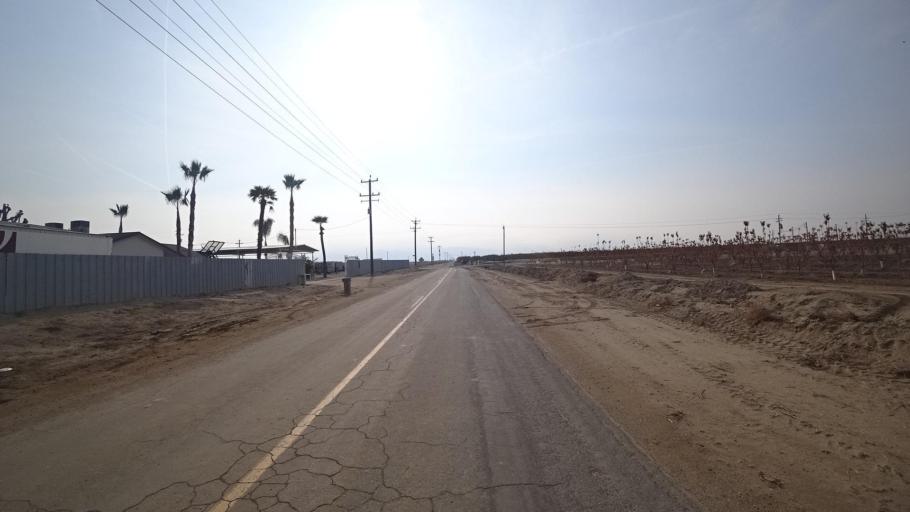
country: US
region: California
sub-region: Kern County
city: Greenfield
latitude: 35.0778
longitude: -119.1006
